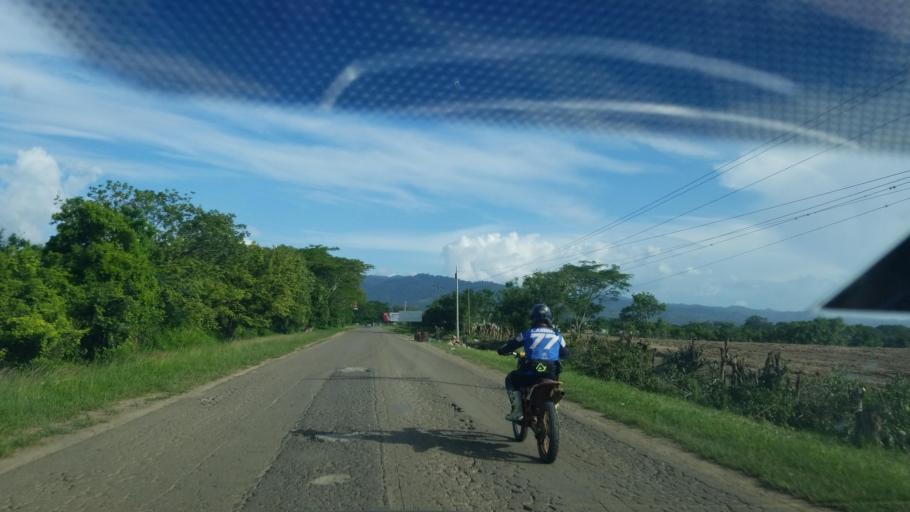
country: HN
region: El Paraiso
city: Cuyali
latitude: 13.9013
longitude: -86.5555
